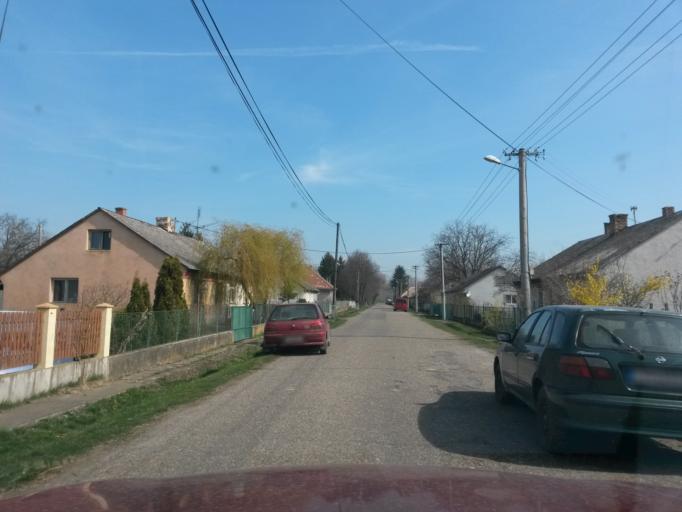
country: SK
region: Nitriansky
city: Levice
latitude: 48.1543
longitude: 18.5766
